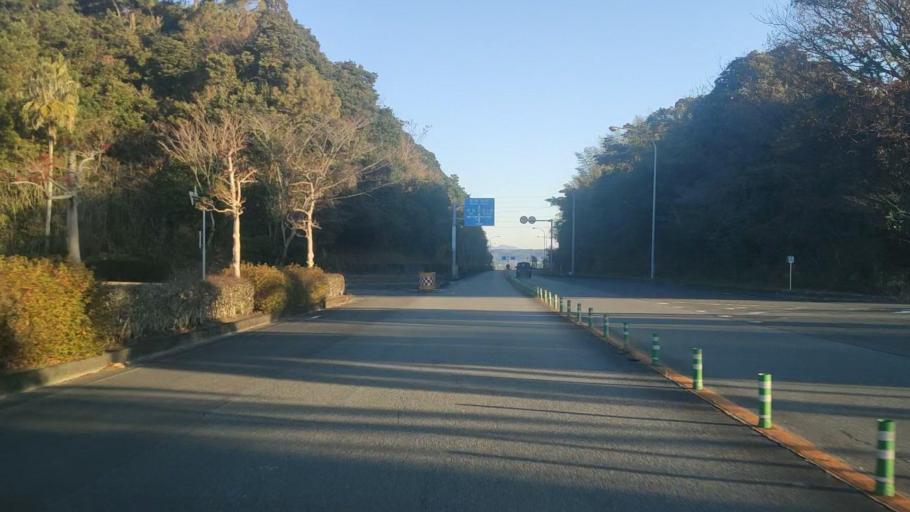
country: JP
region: Miyazaki
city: Tsuma
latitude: 32.0296
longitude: 131.4643
